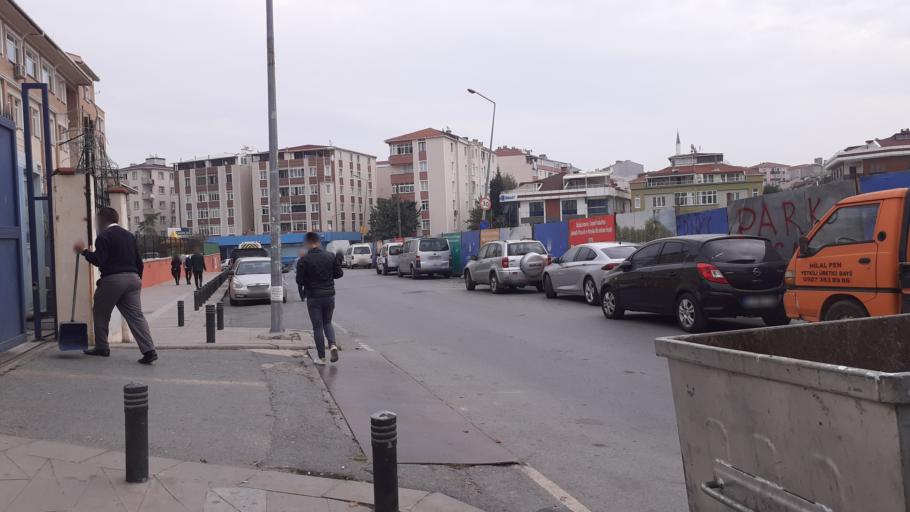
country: TR
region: Istanbul
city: Mahmutbey
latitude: 40.9908
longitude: 28.7828
